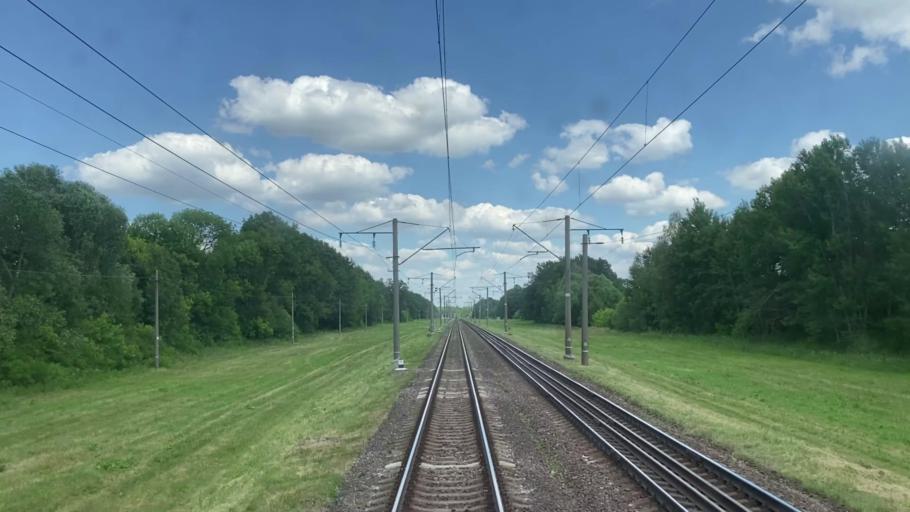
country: BY
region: Brest
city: Zhabinka
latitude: 52.2643
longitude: 24.1428
